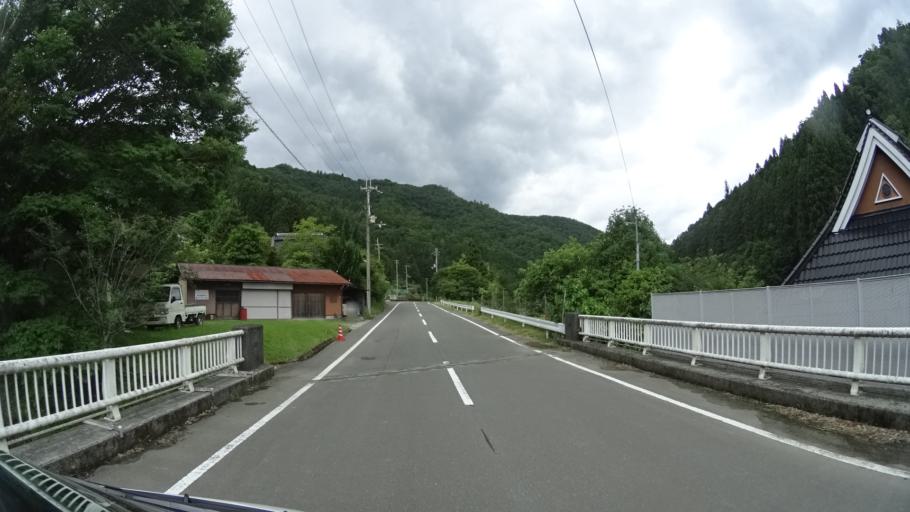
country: JP
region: Hyogo
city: Sasayama
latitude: 35.0559
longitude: 135.3950
